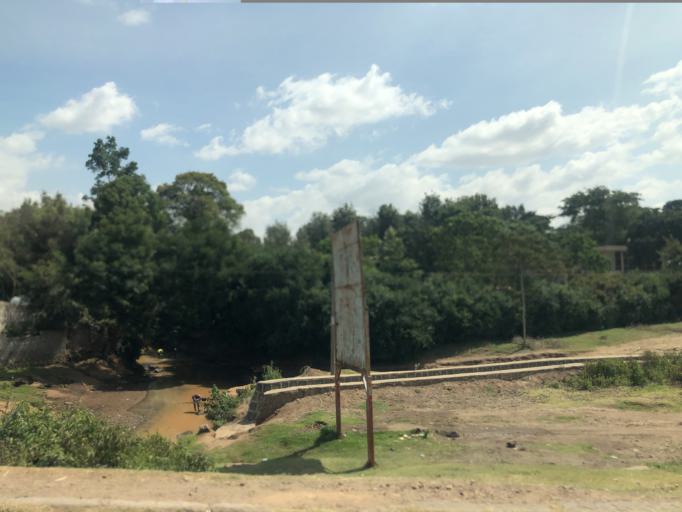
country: ET
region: Oromiya
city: Shashemene
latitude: 7.2139
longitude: 38.6204
